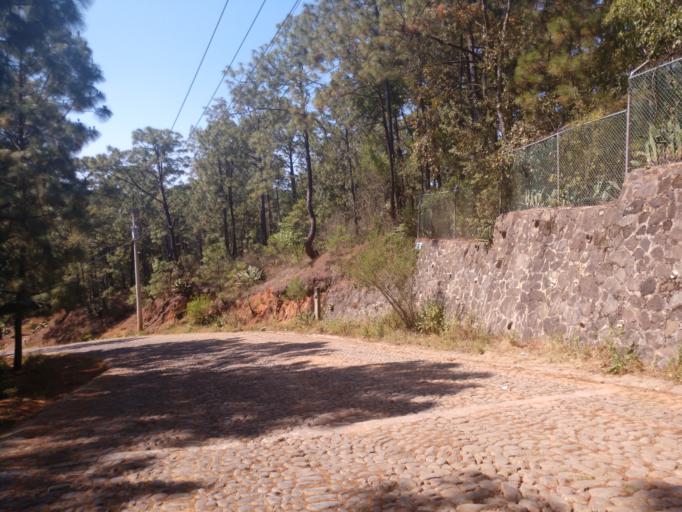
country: MX
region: Jalisco
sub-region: Mazamitla
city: Mazamitla
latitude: 19.9045
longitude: -103.0325
